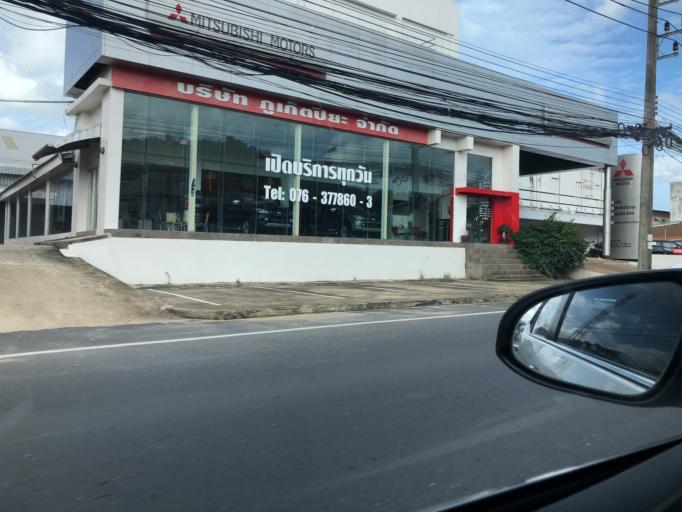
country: TH
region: Phuket
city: Ban Ko Kaeo
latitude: 7.9462
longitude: 98.3928
